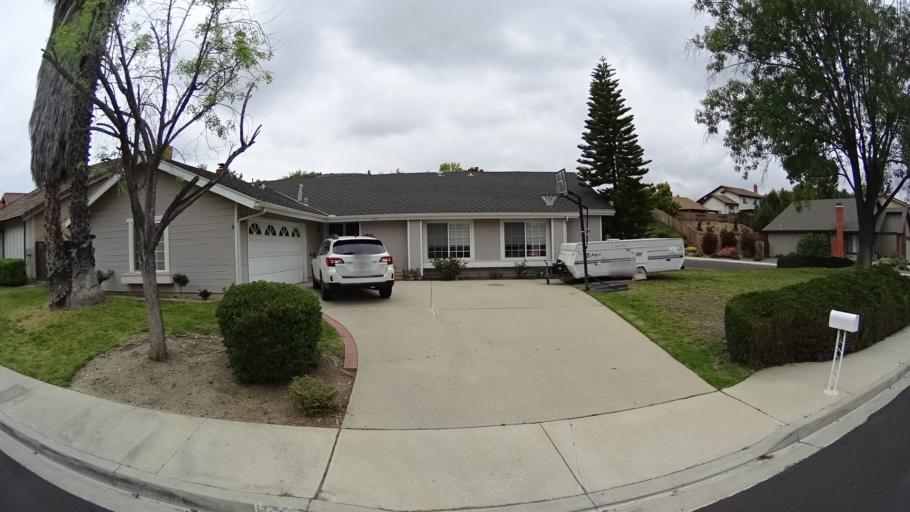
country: US
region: California
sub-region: Ventura County
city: Thousand Oaks
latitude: 34.2184
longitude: -118.8834
